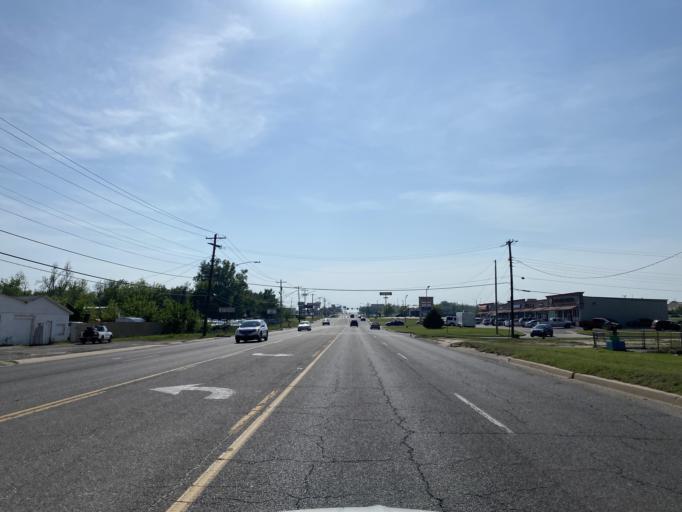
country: US
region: Oklahoma
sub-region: Oklahoma County
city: Spencer
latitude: 35.4931
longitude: -97.3645
